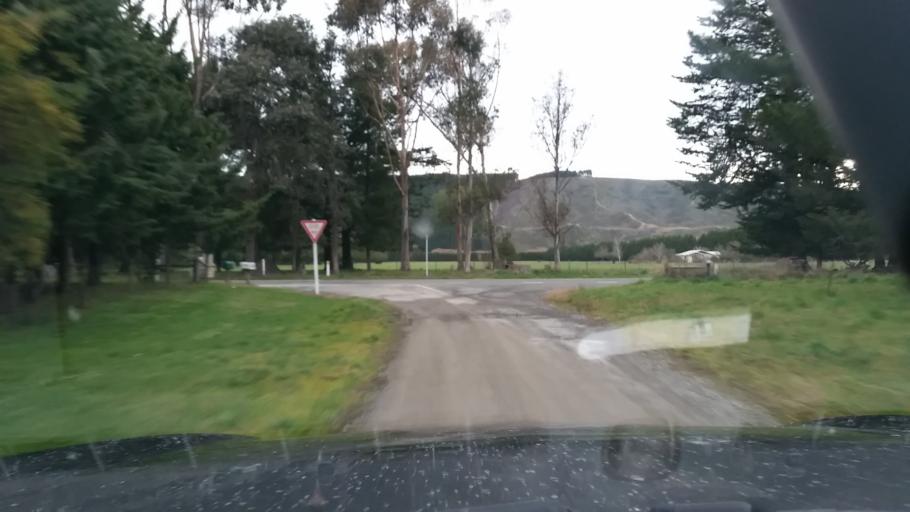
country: NZ
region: Nelson
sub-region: Nelson City
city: Nelson
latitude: -41.5665
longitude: 173.5249
